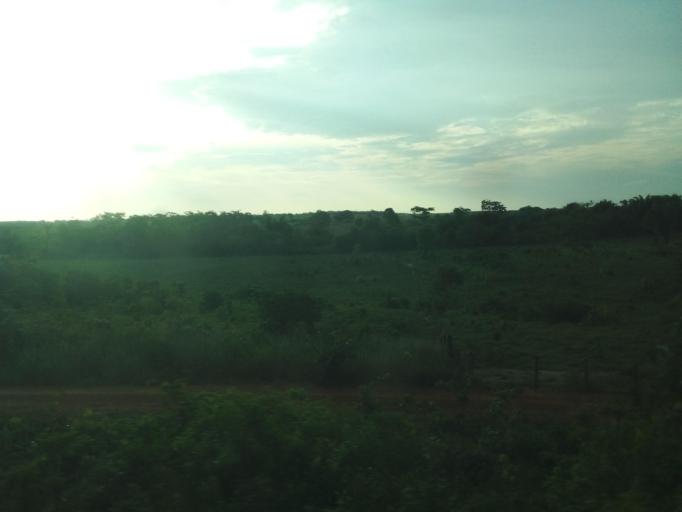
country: BR
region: Maranhao
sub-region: Imperatriz
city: Imperatriz
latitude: -4.8264
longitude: -47.3651
